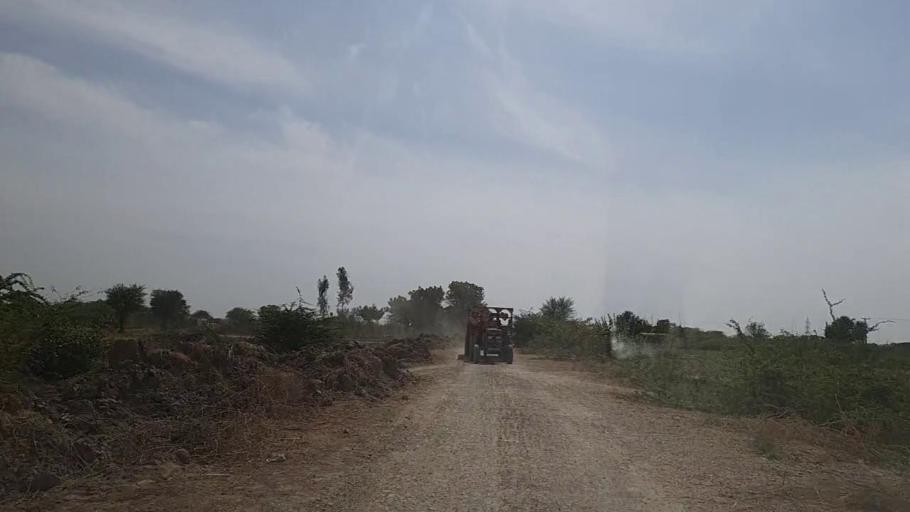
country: PK
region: Sindh
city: Samaro
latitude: 25.2011
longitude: 69.4637
